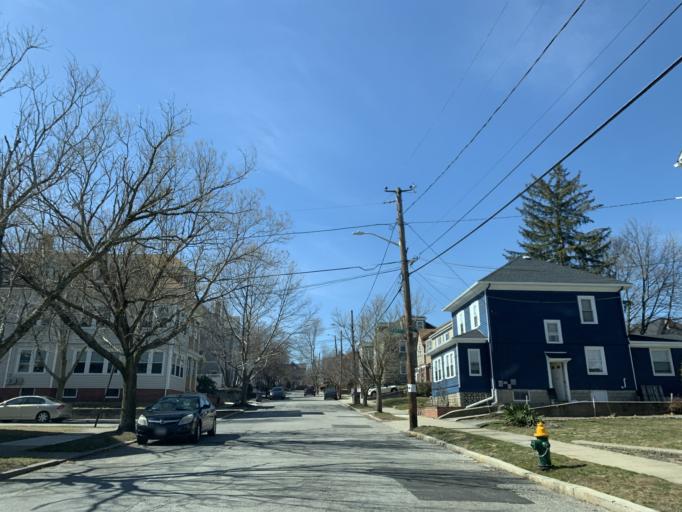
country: US
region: Rhode Island
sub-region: Providence County
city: Providence
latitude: 41.8439
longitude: -71.3947
